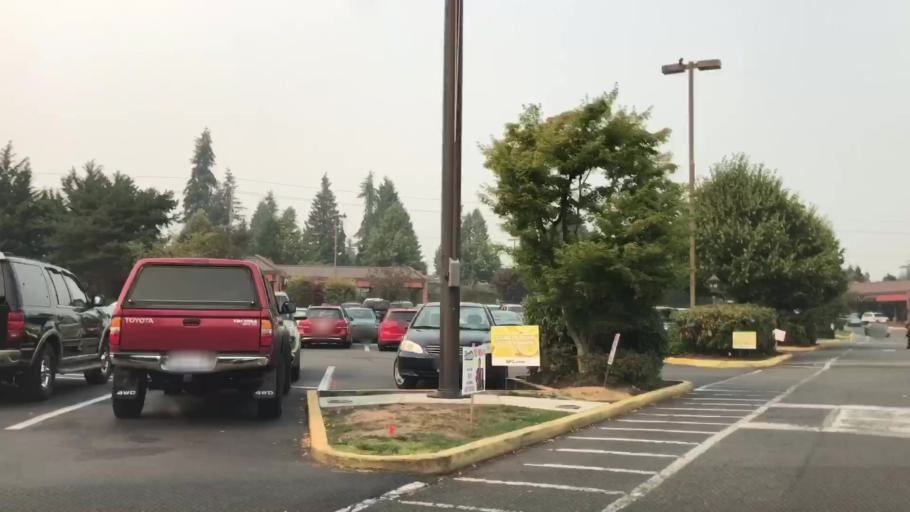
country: US
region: Washington
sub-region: Snohomish County
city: Mountlake Terrace
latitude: 47.7906
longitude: -122.2911
